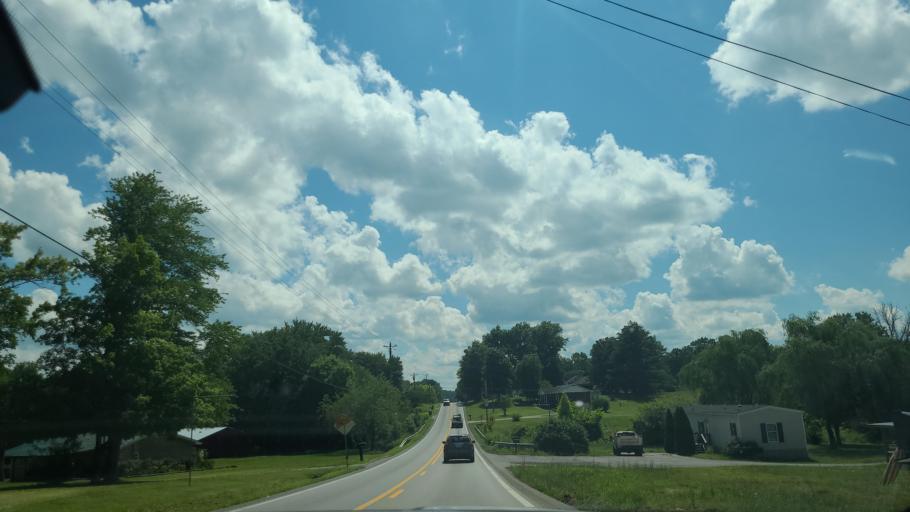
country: US
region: Kentucky
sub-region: Whitley County
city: Corbin
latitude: 36.9068
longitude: -84.1587
